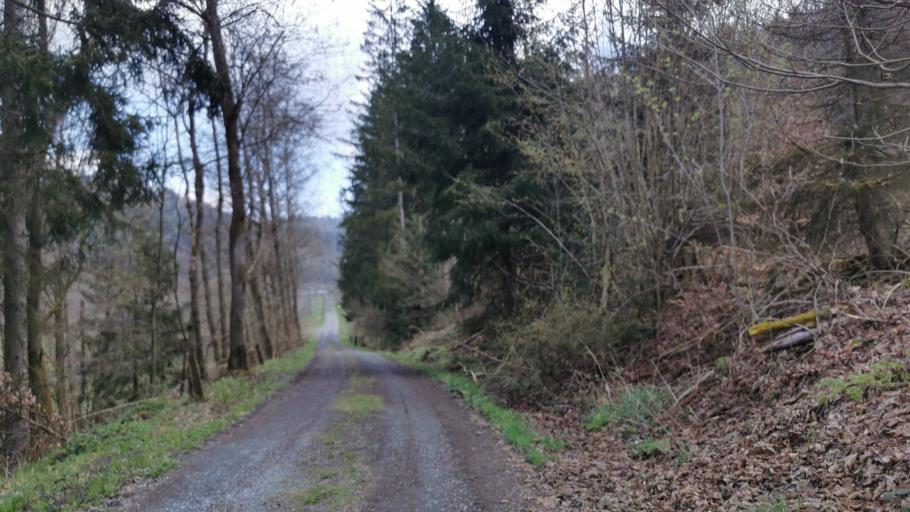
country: DE
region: Bavaria
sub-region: Upper Franconia
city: Pressig
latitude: 50.3685
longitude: 11.3285
